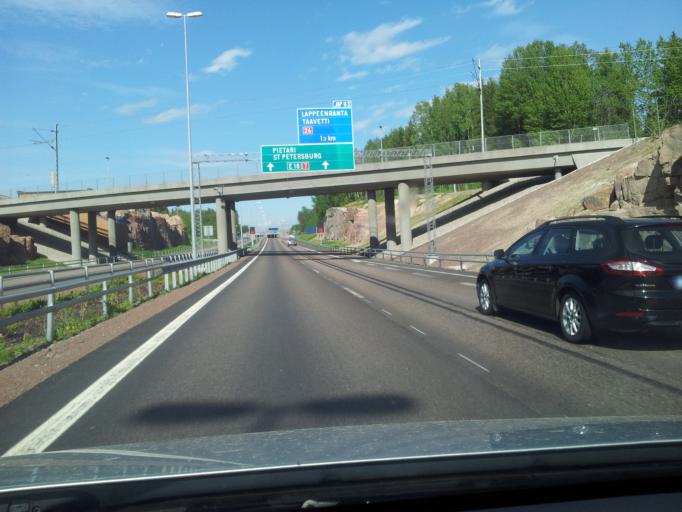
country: FI
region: Kymenlaakso
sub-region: Kotka-Hamina
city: Hamina
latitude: 60.5904
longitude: 27.1615
